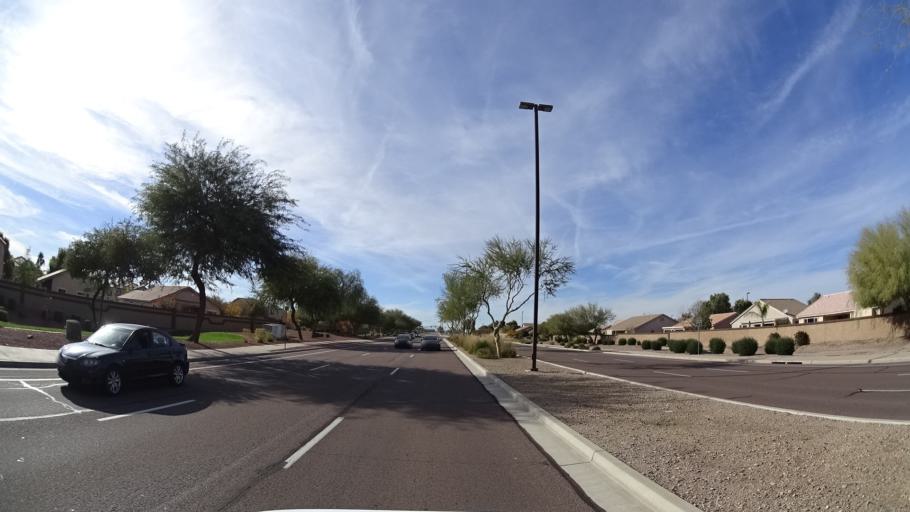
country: US
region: Arizona
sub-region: Maricopa County
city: Queen Creek
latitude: 33.2776
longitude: -111.7168
